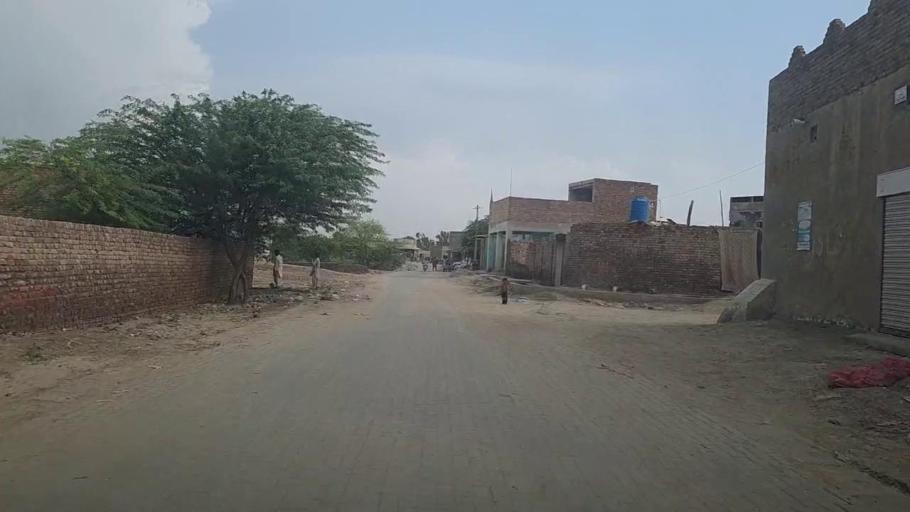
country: PK
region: Sindh
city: Mirpur Mathelo
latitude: 27.9184
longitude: 69.5212
